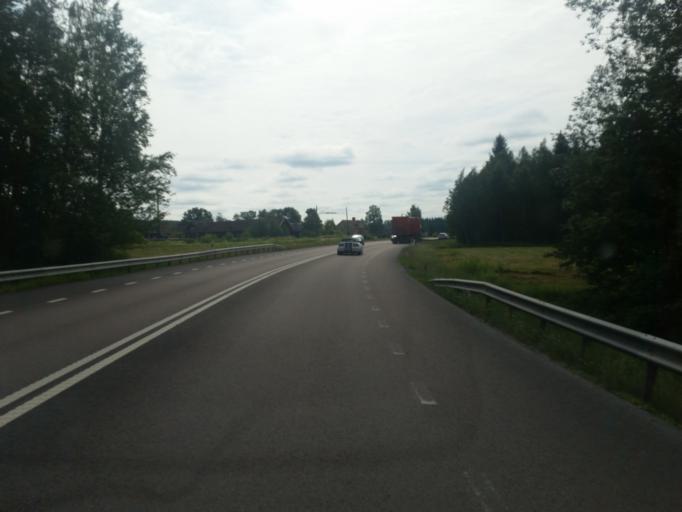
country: SE
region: Dalarna
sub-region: Gagnefs Kommun
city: Djuras
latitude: 60.5785
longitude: 15.1207
